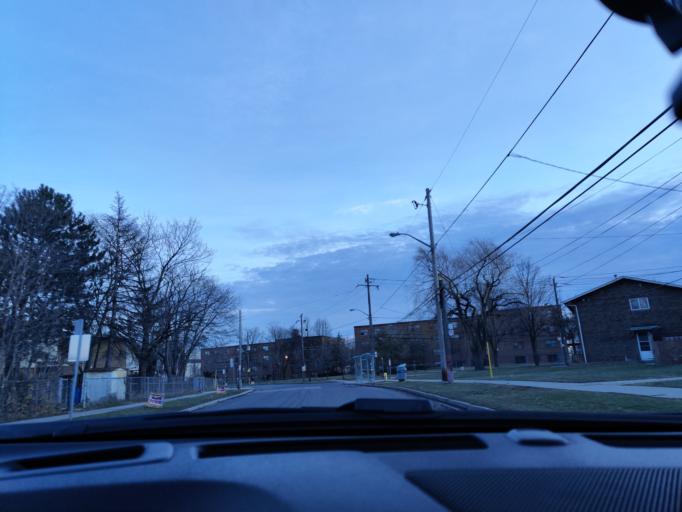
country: CA
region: Ontario
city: Toronto
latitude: 43.7196
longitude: -79.4488
